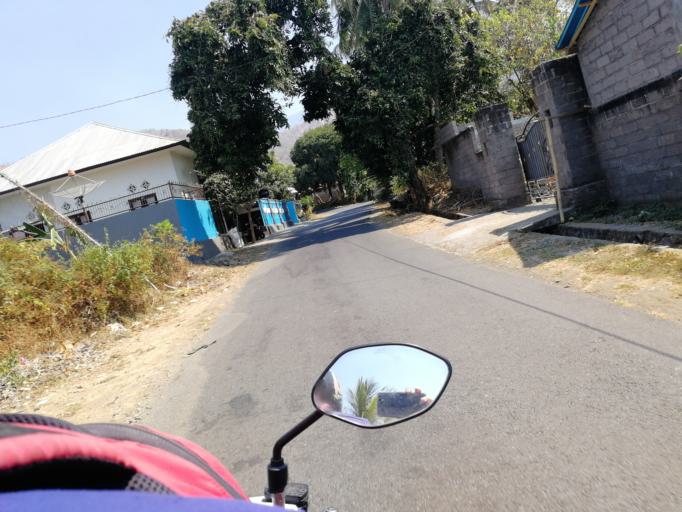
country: ID
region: Bali
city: Banjar Trunyan
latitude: -8.1242
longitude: 115.3287
